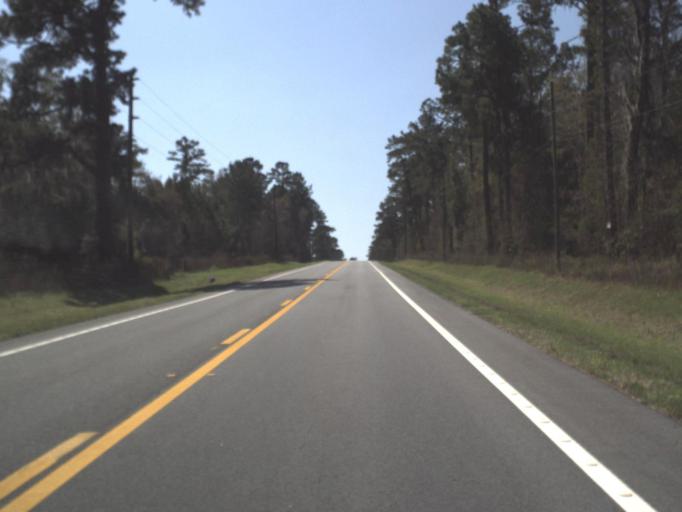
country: US
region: Florida
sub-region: Jefferson County
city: Monticello
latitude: 30.4156
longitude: -84.0205
